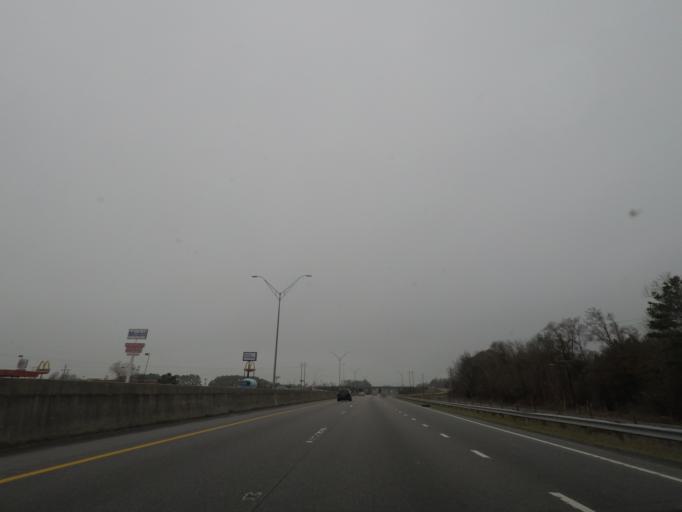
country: US
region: North Carolina
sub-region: Robeson County
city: Lumberton
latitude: 34.6246
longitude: -79.0471
